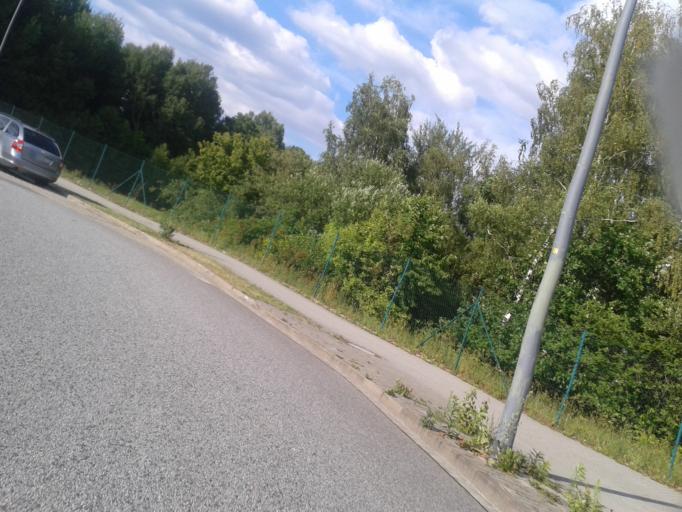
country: DE
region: Saxony
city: Albertstadt
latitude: 51.1285
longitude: 13.7778
